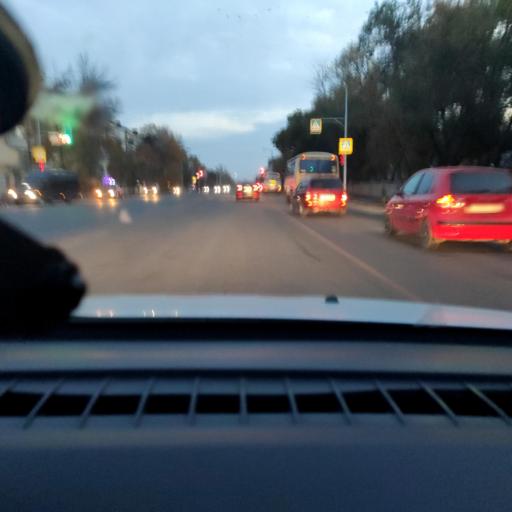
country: RU
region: Samara
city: Samara
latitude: 53.1183
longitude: 50.0860
